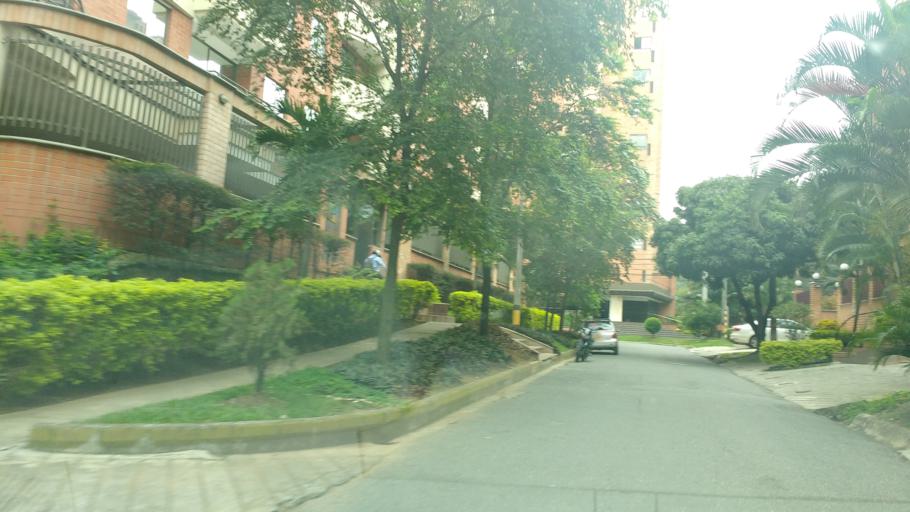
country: CO
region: Antioquia
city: Medellin
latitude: 6.2431
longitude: -75.5834
